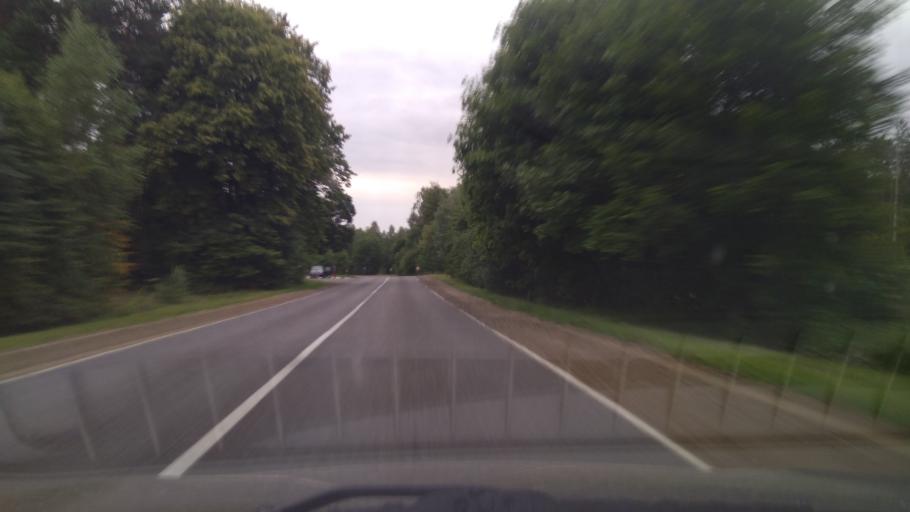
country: BY
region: Brest
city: Byaroza
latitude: 52.4118
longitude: 24.9921
